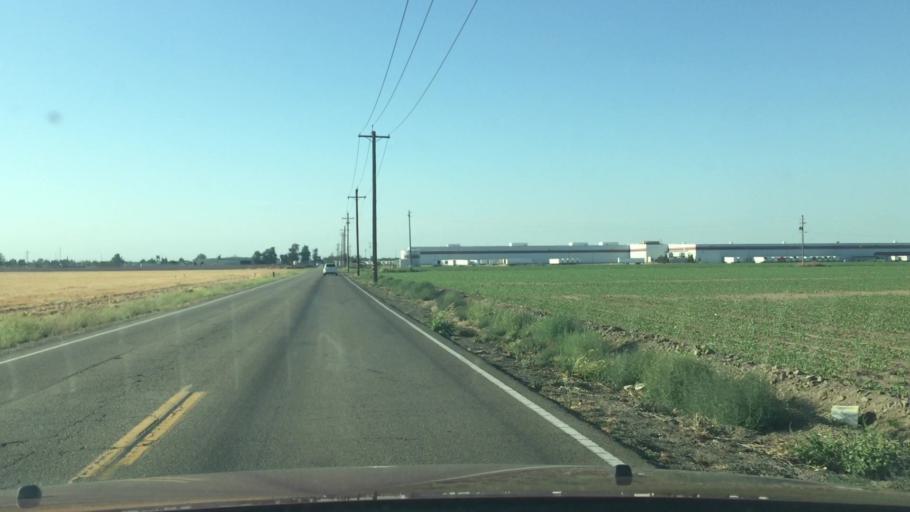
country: US
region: California
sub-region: San Joaquin County
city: Lathrop
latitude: 37.8002
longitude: -121.2707
